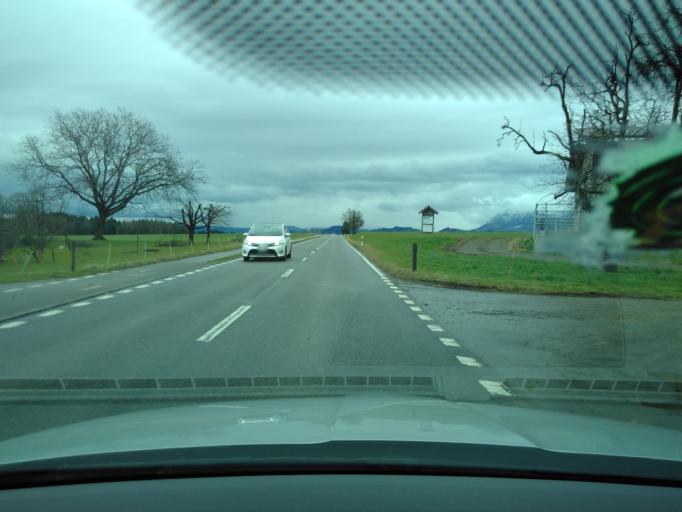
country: CH
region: Lucerne
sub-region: Hochdorf District
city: Hochdorf
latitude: 47.1289
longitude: 8.2896
